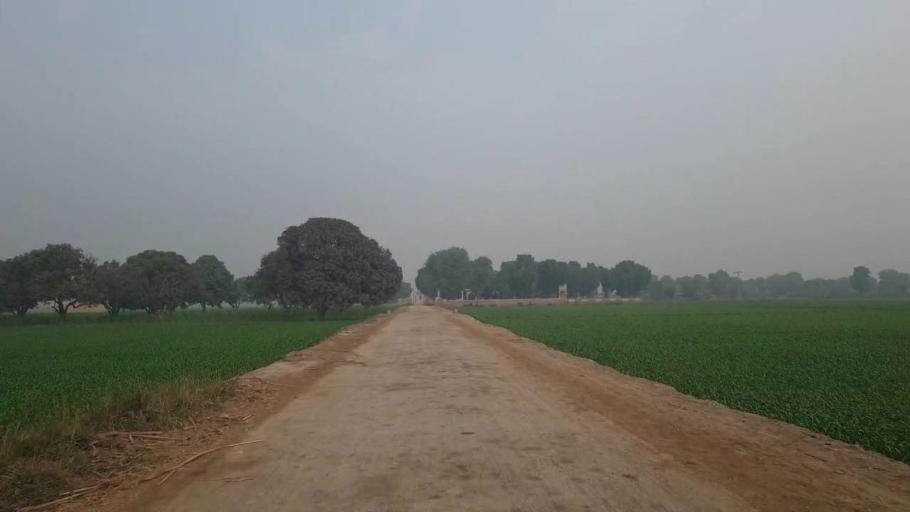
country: PK
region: Sindh
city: Tando Adam
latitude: 25.7108
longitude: 68.6594
